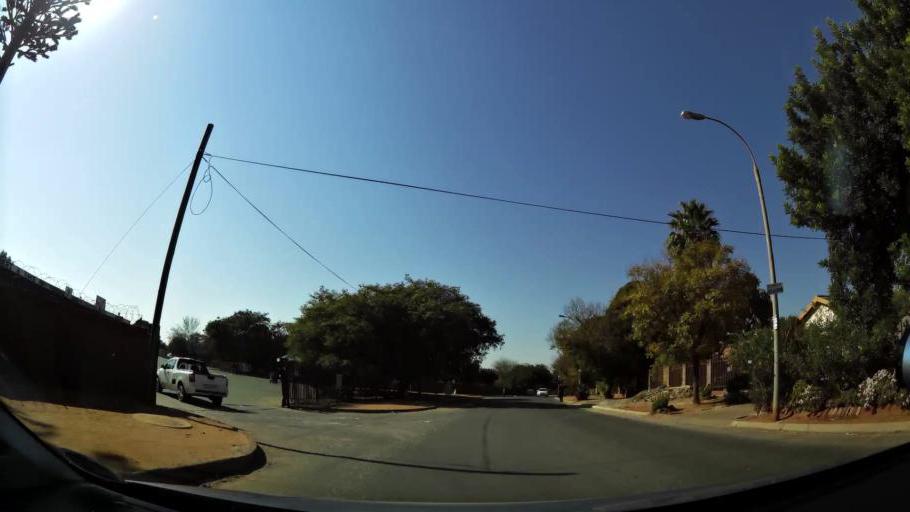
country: ZA
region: Gauteng
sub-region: Ekurhuleni Metropolitan Municipality
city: Tembisa
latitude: -26.0481
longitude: 28.2060
